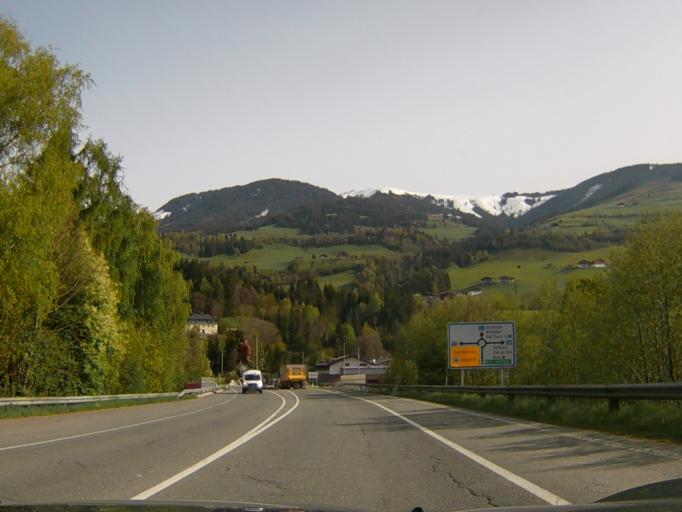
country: AT
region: Salzburg
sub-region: Politischer Bezirk Zell am See
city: Mittersill
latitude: 47.2789
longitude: 12.4884
